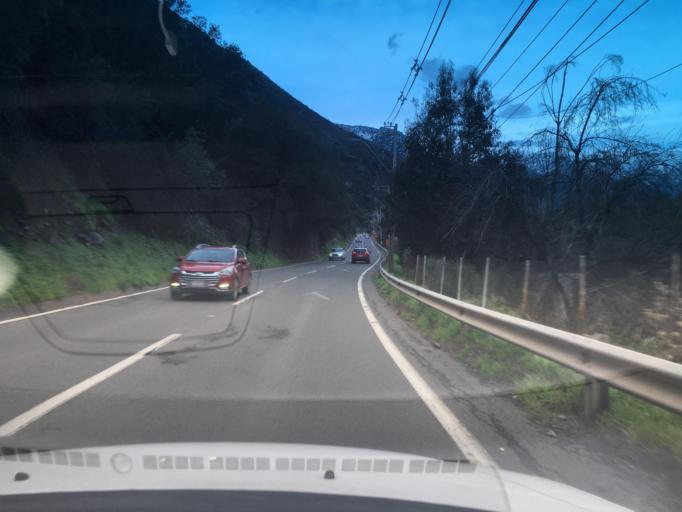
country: CL
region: Santiago Metropolitan
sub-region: Provincia de Cordillera
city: Puente Alto
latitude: -33.5778
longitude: -70.4322
